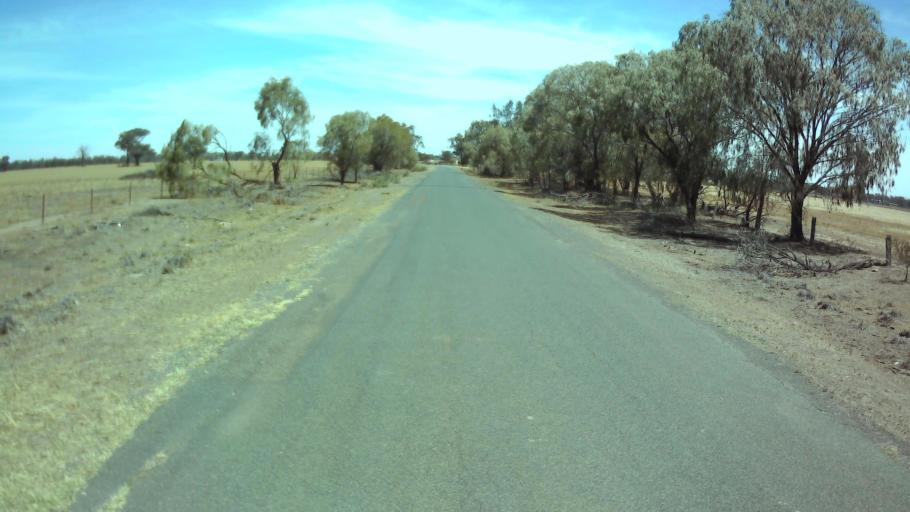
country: AU
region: New South Wales
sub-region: Weddin
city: Grenfell
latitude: -33.8285
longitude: 147.7462
